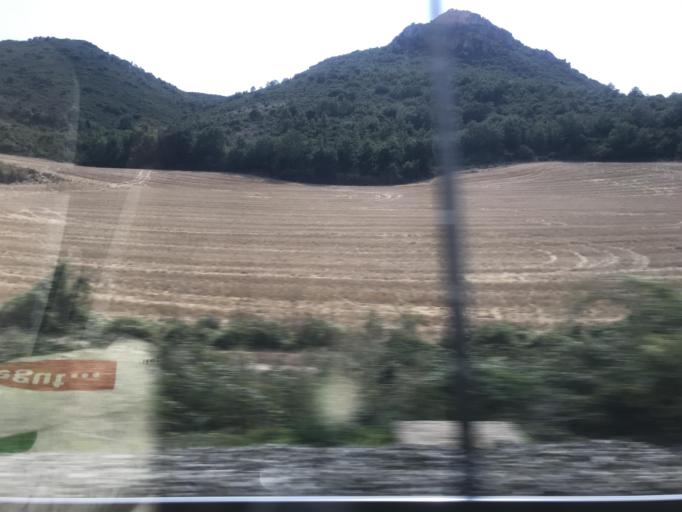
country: ES
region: Castille and Leon
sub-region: Provincia de Burgos
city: Bugedo
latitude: 42.6504
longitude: -3.0005
